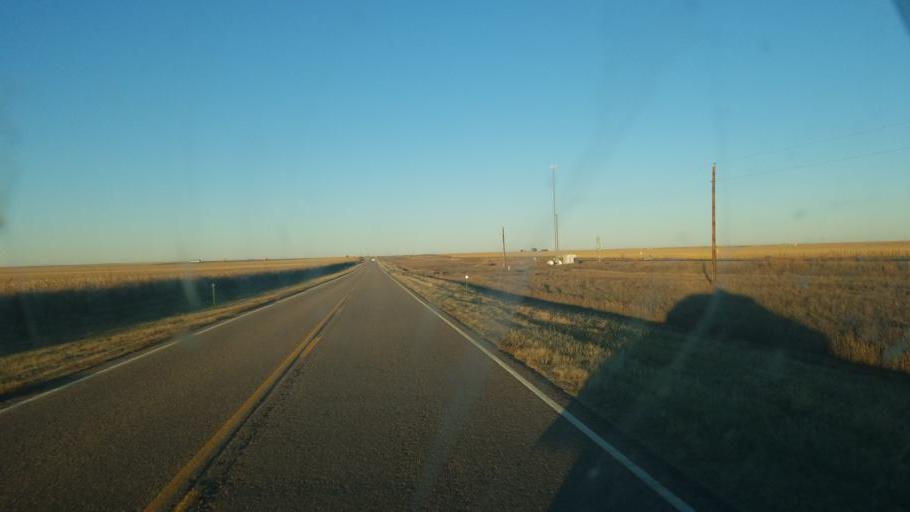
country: US
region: Colorado
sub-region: Cheyenne County
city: Cheyenne Wells
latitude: 38.8508
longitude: -102.0911
